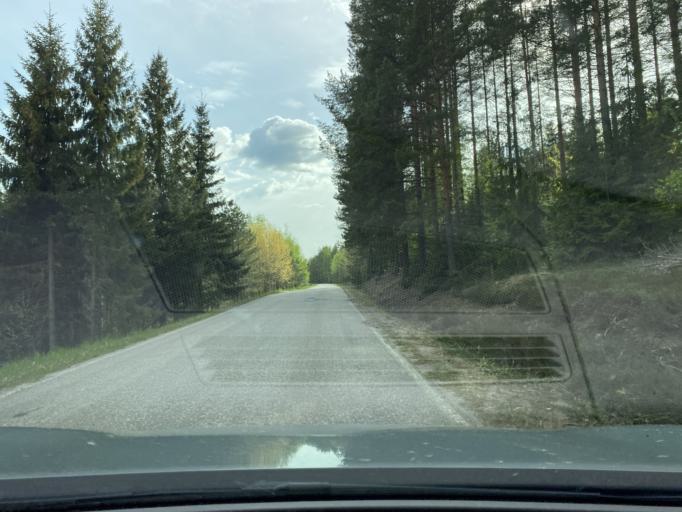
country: FI
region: Varsinais-Suomi
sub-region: Salo
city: Kiikala
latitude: 60.4812
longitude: 23.5387
